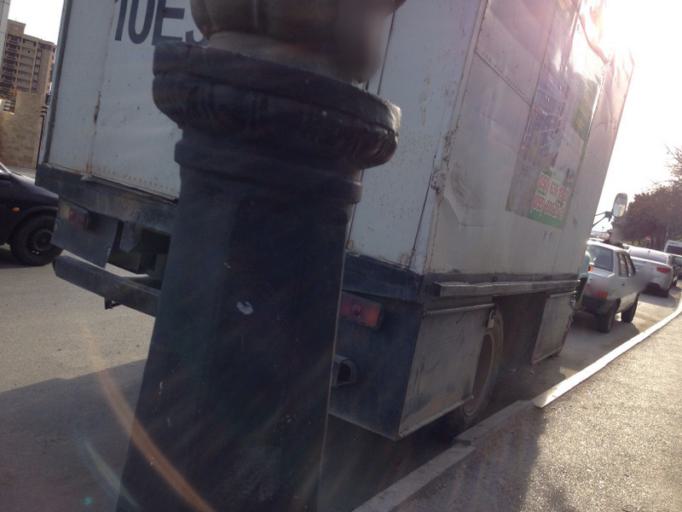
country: AZ
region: Baki
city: Baku
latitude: 40.3837
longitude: 49.8524
